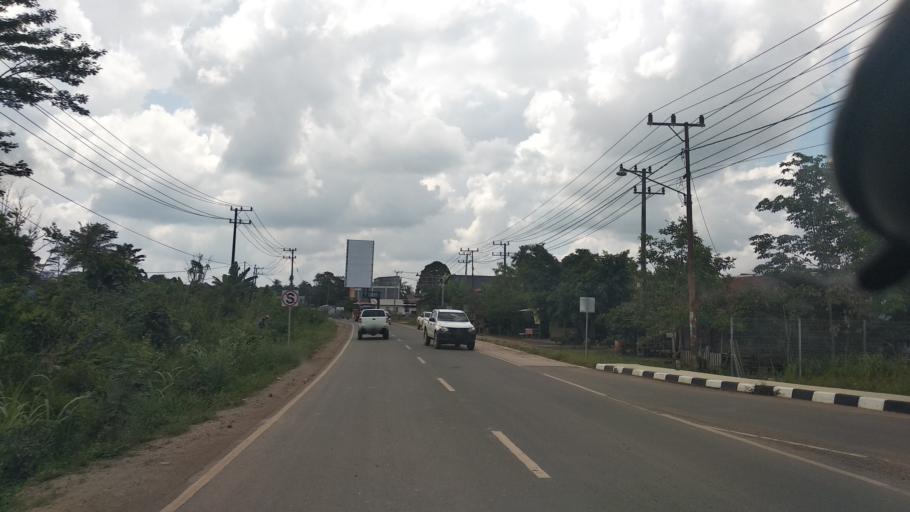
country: ID
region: East Kalimantan
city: Samarinda
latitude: -0.3738
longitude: 117.2646
